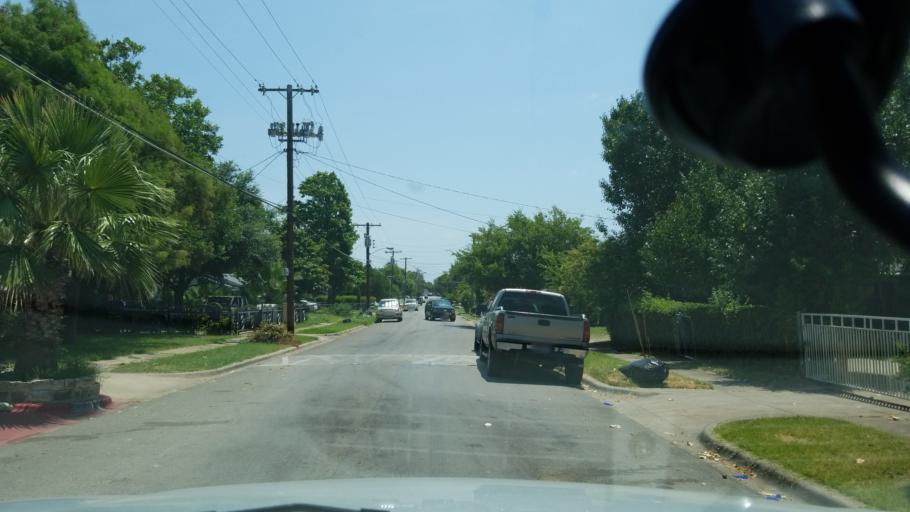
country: US
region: Texas
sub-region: Dallas County
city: Cockrell Hill
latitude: 32.7168
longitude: -96.8612
